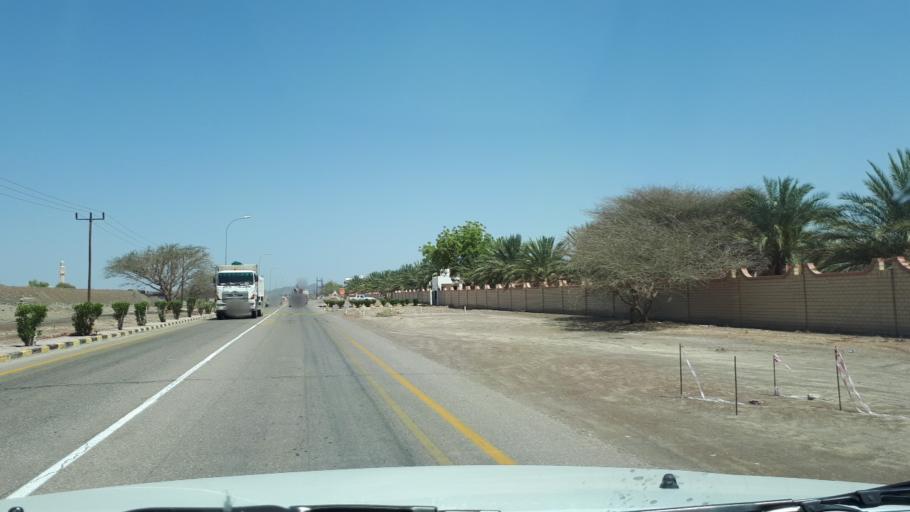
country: OM
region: Ash Sharqiyah
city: Al Qabil
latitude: 22.6095
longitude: 58.6653
